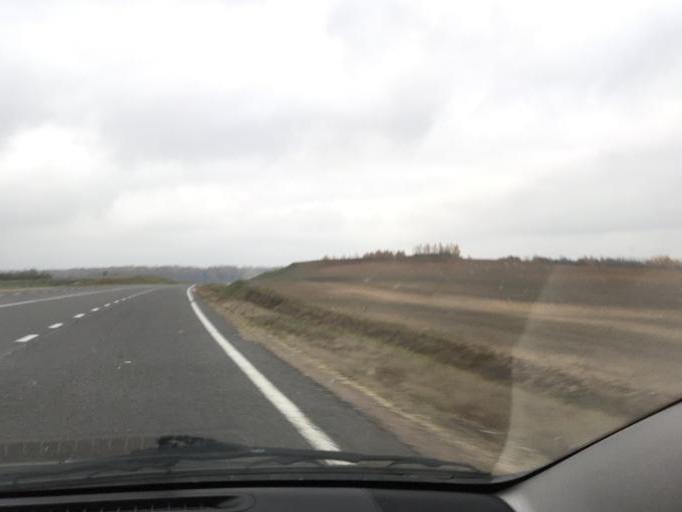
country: BY
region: Vitebsk
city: Vitebsk
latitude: 55.1586
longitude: 30.0656
